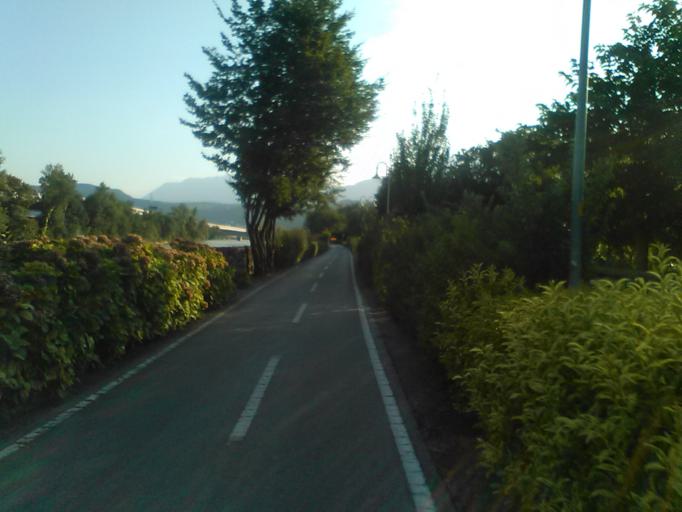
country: IT
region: Trentino-Alto Adige
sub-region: Bolzano
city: Bolzano
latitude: 46.4857
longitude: 11.3280
